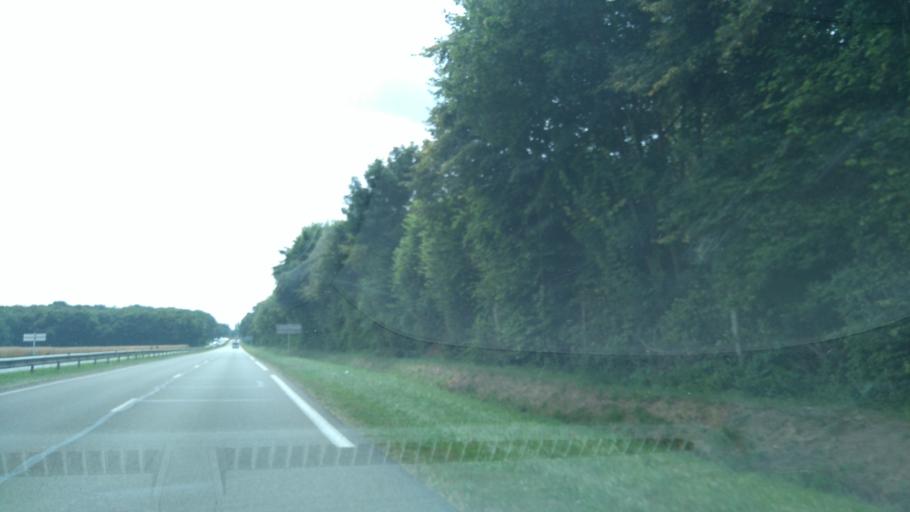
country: FR
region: Picardie
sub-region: Departement de l'Oise
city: Saint-Maximin
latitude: 49.2168
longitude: 2.4657
